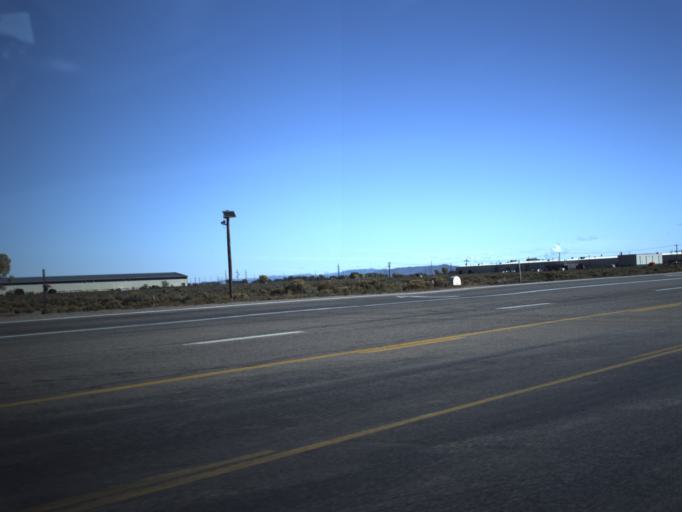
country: US
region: Utah
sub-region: Iron County
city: Cedar City
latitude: 37.6847
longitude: -113.1617
